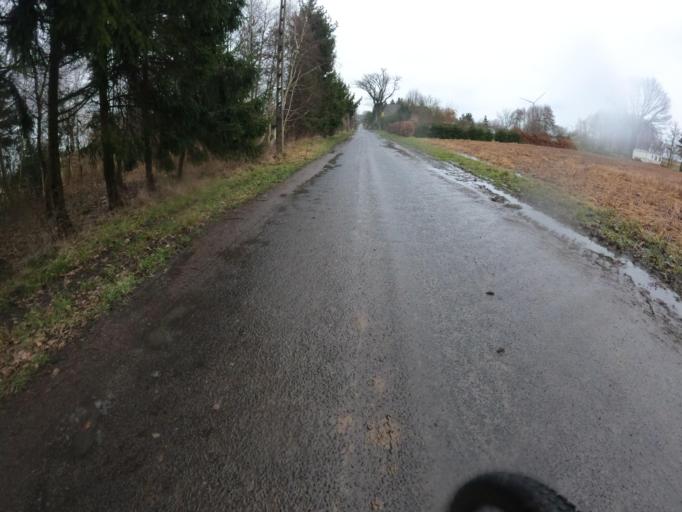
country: PL
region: West Pomeranian Voivodeship
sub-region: Powiat slawienski
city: Darlowo
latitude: 54.3939
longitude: 16.5269
